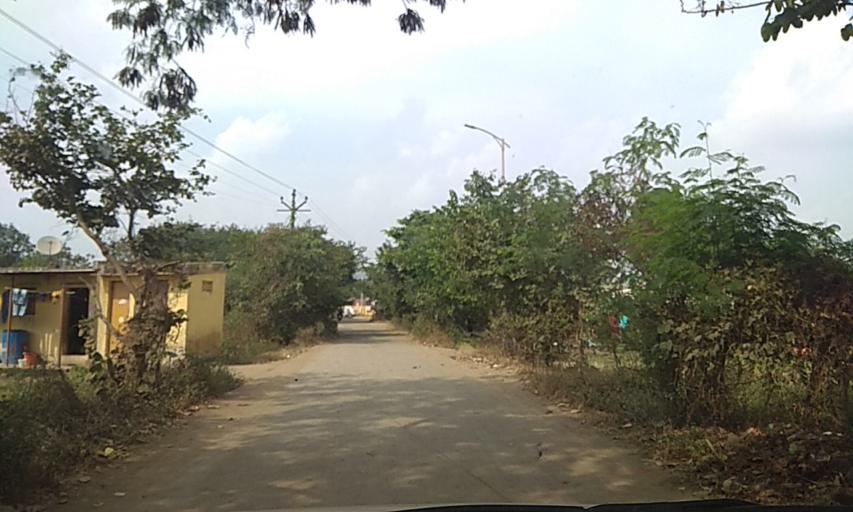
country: IN
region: Maharashtra
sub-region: Pune Division
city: Pimpri
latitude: 18.5816
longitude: 73.7070
